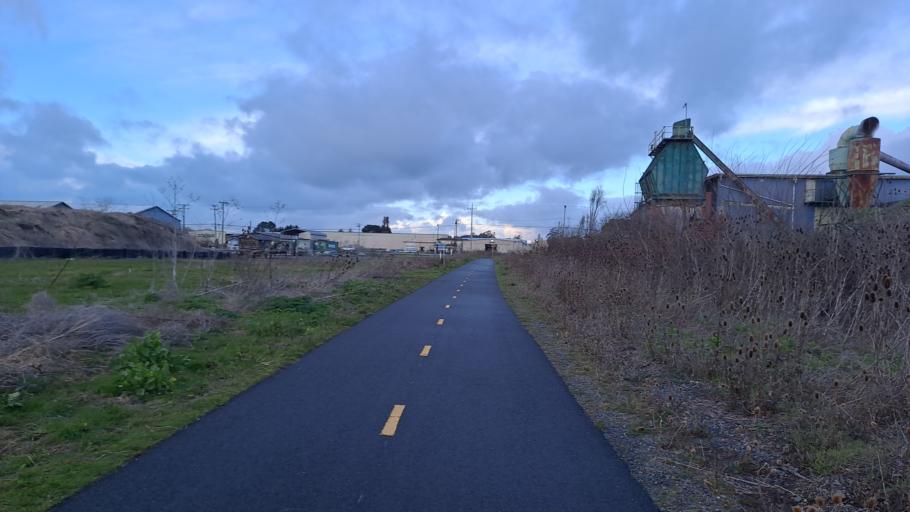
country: US
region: California
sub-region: Humboldt County
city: Arcata
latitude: 40.8645
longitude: -124.0930
